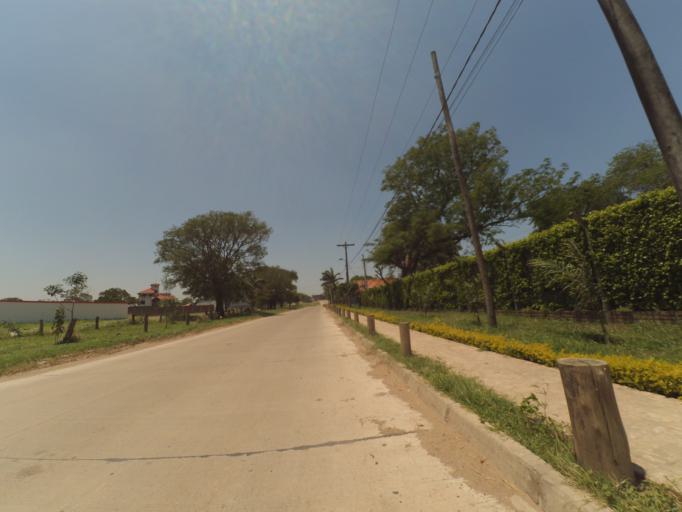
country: BO
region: Santa Cruz
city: Santa Cruz de la Sierra
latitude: -17.8452
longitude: -63.2434
